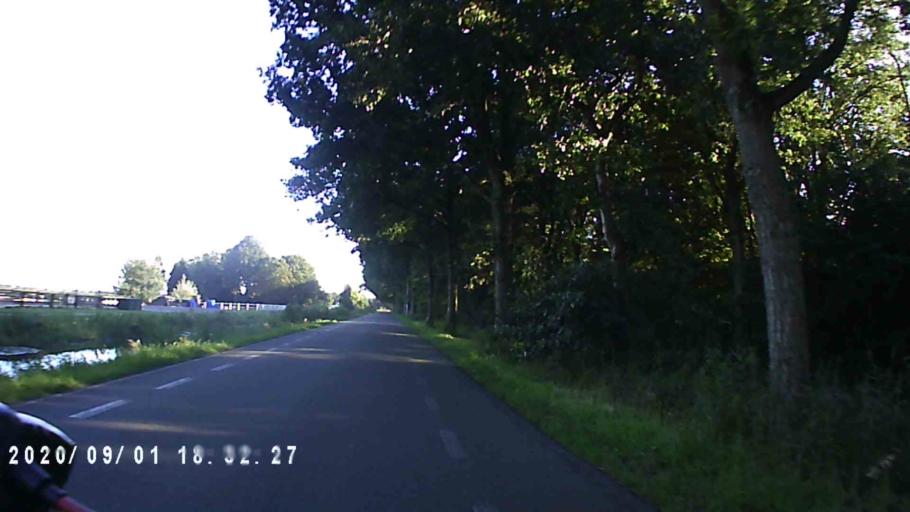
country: NL
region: Groningen
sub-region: Gemeente Hoogezand-Sappemeer
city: Sappemeer
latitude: 53.1528
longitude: 6.7966
